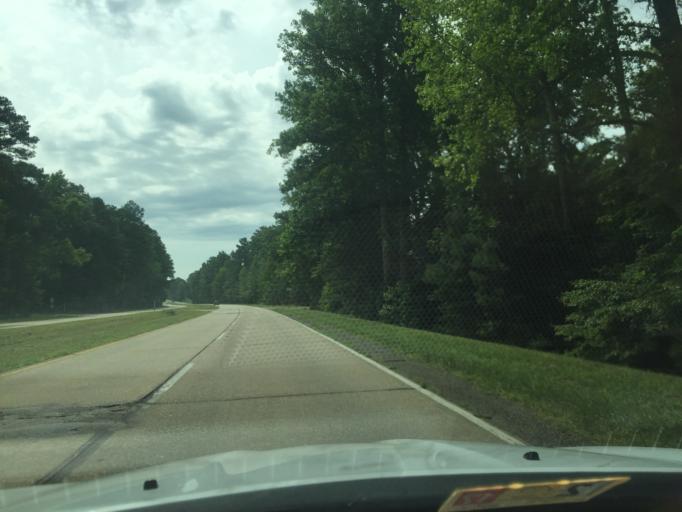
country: US
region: Virginia
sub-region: Charles City County
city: Charles City
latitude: 37.4597
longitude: -77.0985
